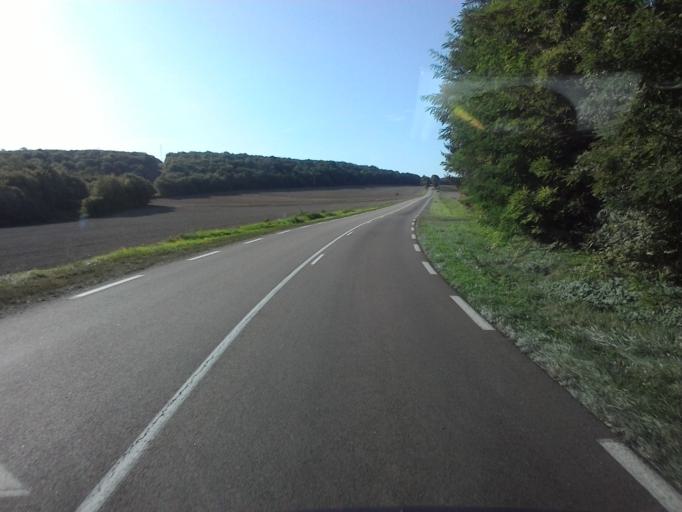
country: FR
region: Champagne-Ardenne
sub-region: Departement de l'Aube
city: Mussy-sur-Seine
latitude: 48.0108
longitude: 4.4742
